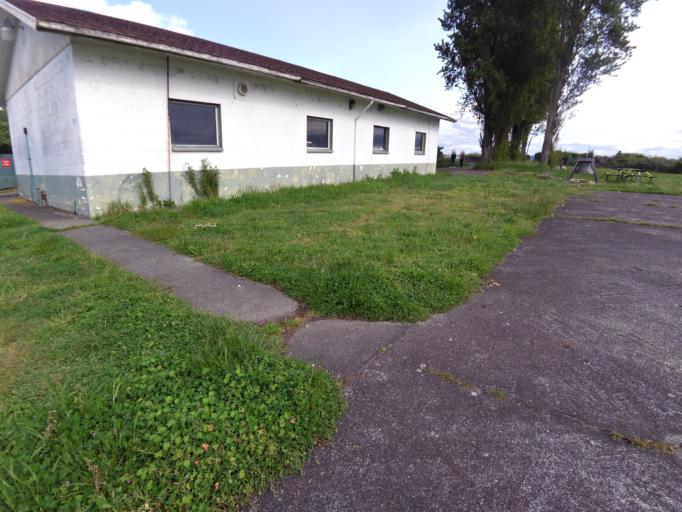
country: US
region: Washington
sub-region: Kitsap County
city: Bainbridge Island
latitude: 47.6621
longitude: -122.4345
